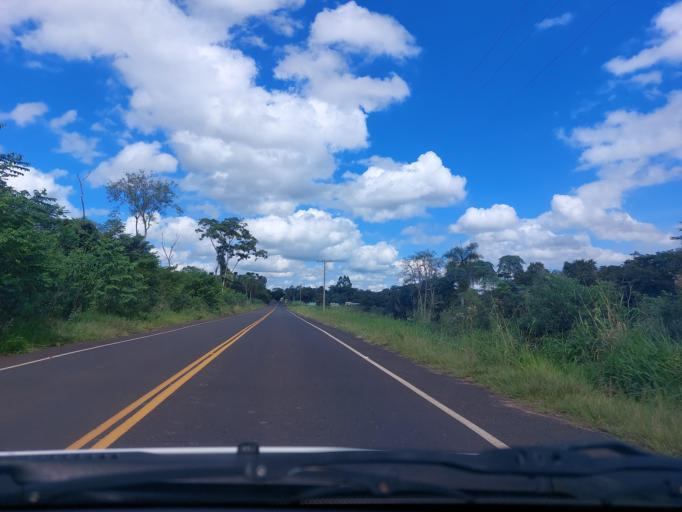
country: PY
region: San Pedro
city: Guayaybi
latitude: -24.5628
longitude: -56.5196
